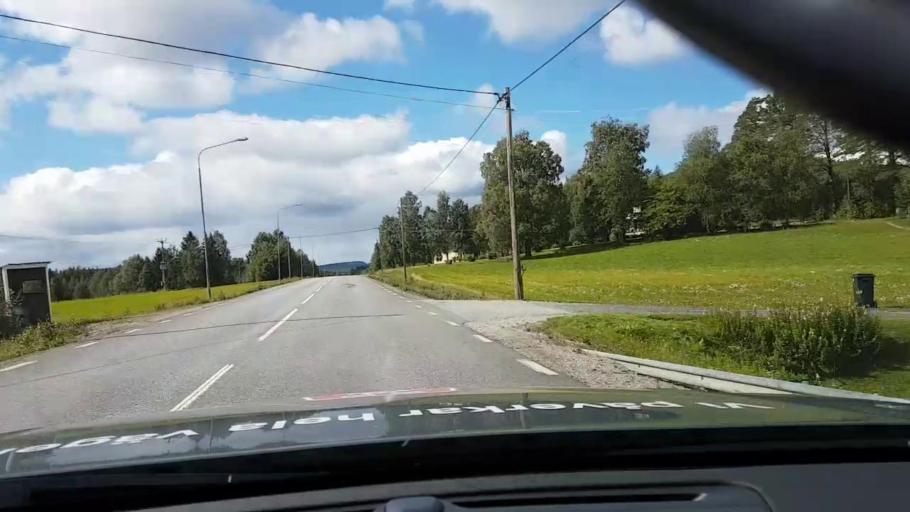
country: SE
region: Vaesternorrland
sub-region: OErnskoeldsviks Kommun
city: Bredbyn
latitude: 63.5264
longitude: 18.0303
